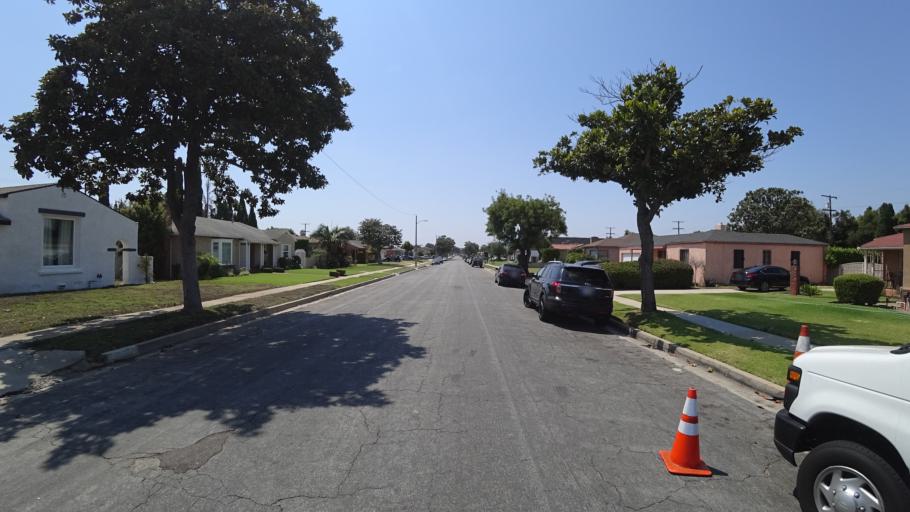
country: US
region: California
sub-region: Los Angeles County
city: Westmont
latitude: 33.9560
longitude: -118.3233
